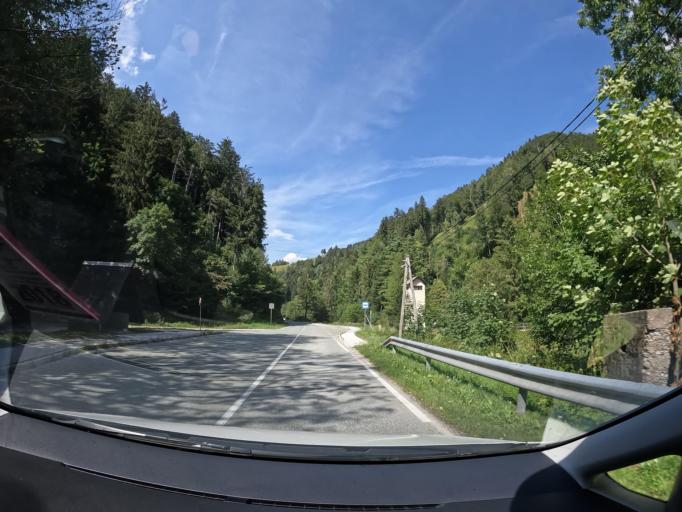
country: SI
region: Preddvor
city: Preddvor
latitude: 46.3735
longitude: 14.4037
